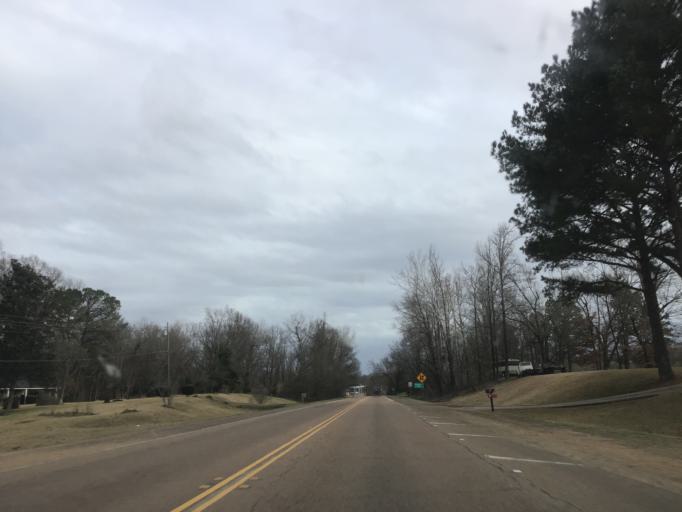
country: US
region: Mississippi
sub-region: Warren County
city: Beechwood
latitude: 32.3397
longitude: -90.8269
